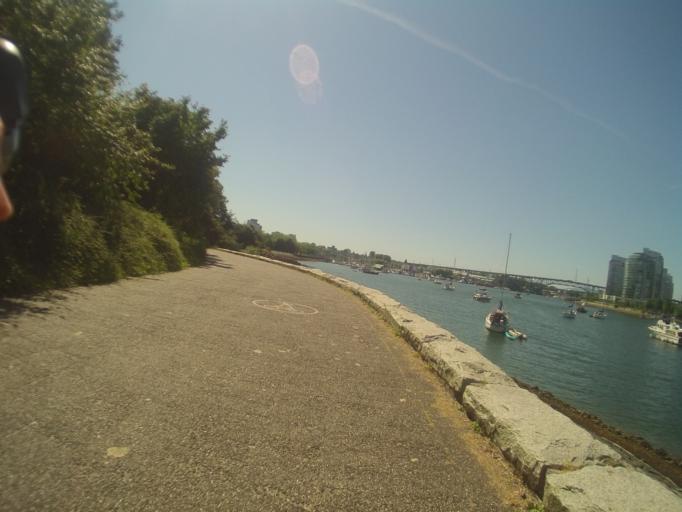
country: CA
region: British Columbia
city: West End
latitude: 49.2685
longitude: -123.1218
